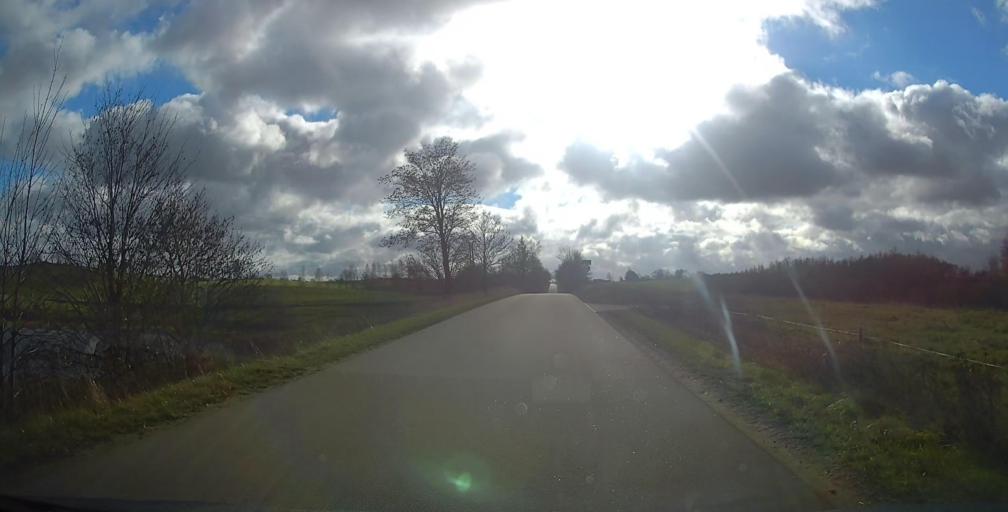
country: PL
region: Podlasie
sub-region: Suwalki
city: Suwalki
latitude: 54.3242
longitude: 22.8623
